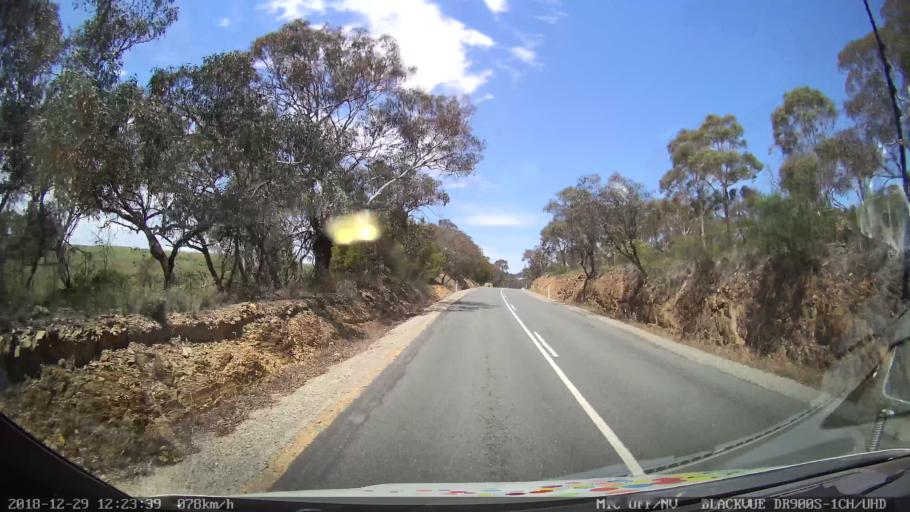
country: AU
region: New South Wales
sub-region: Queanbeyan
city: Queanbeyan
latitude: -35.4390
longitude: 149.2159
